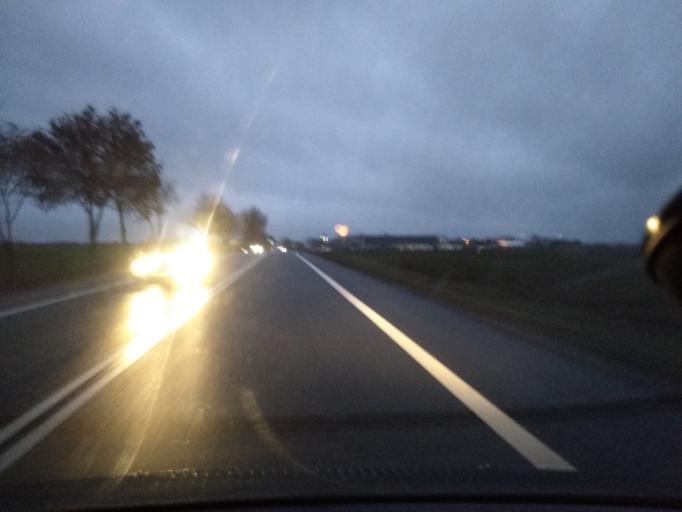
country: PL
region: Lower Silesian Voivodeship
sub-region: Powiat sredzki
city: Szczepanow
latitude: 51.1644
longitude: 16.6505
